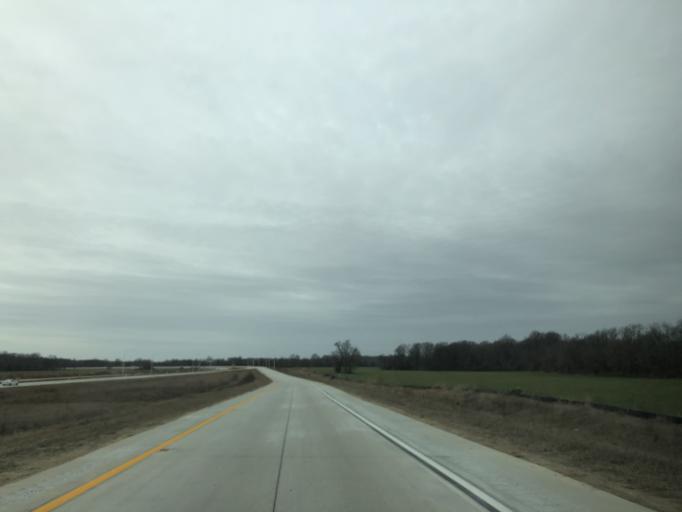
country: US
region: Delaware
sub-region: New Castle County
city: Middletown
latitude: 39.5248
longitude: -75.6807
